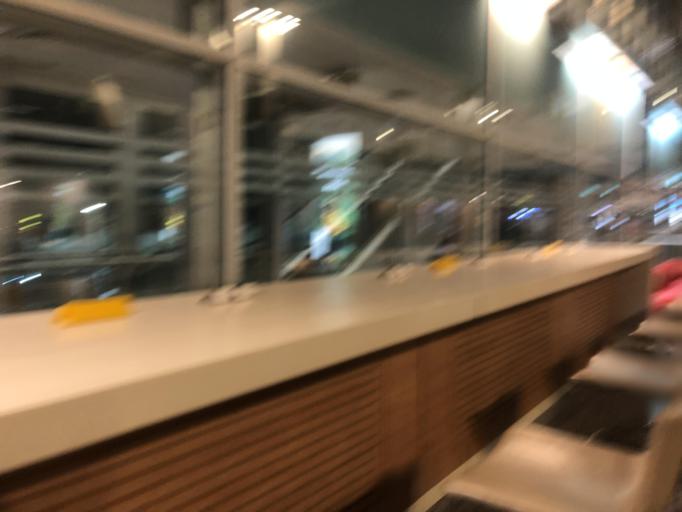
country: IN
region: Karnataka
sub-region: Bangalore Rural
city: Devanhalli
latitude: 13.2013
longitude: 77.7103
